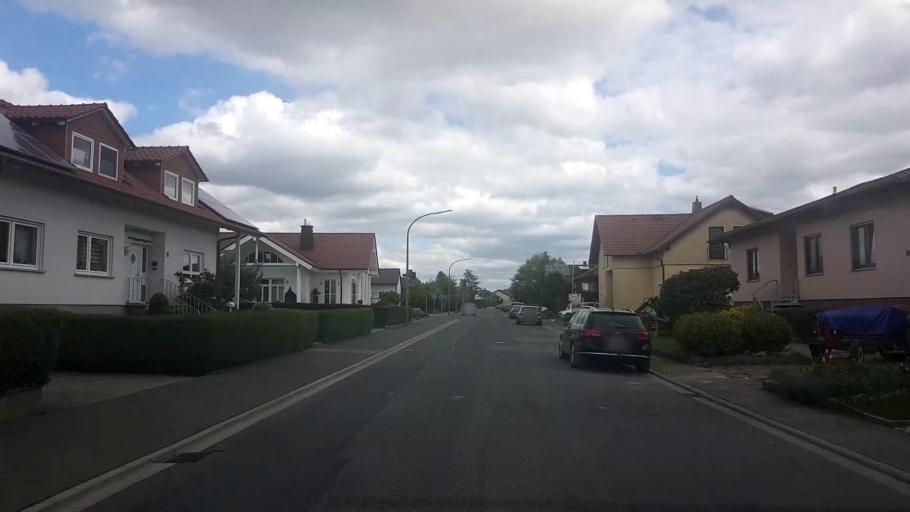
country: DE
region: Bavaria
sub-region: Upper Franconia
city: Lichtenfels
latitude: 50.1295
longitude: 11.0263
